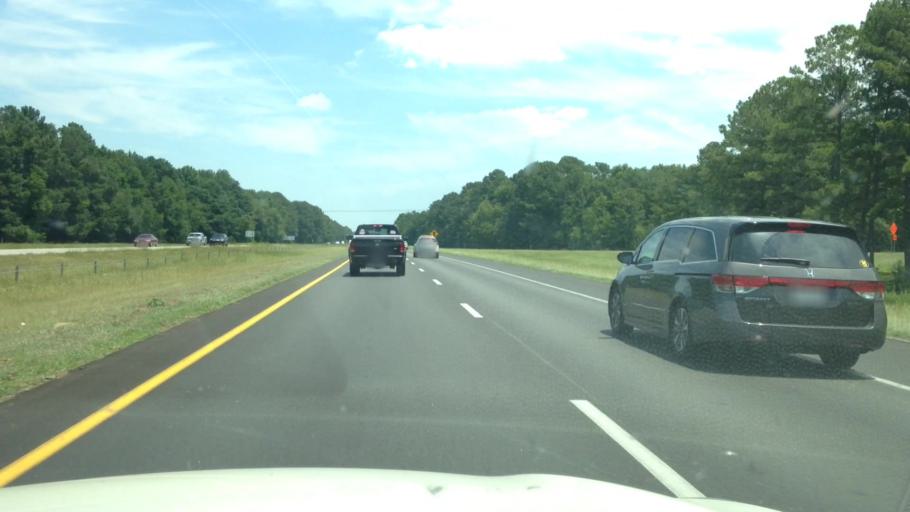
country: US
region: South Carolina
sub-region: Lee County
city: Bishopville
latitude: 34.1897
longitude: -80.1652
